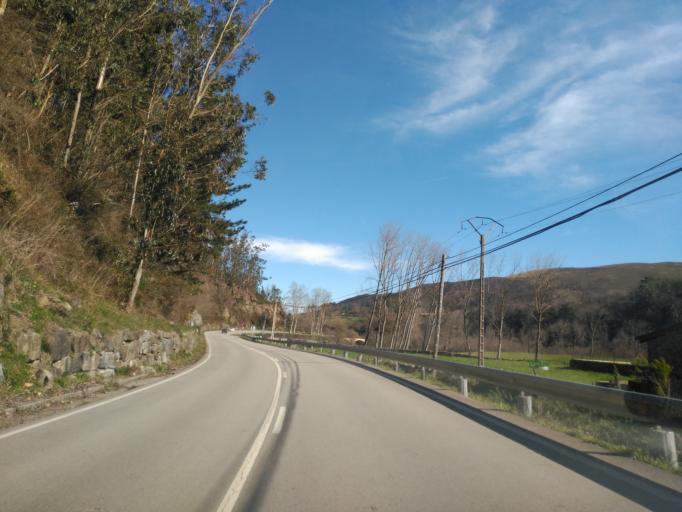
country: ES
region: Cantabria
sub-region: Provincia de Cantabria
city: Ruente
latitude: 43.2350
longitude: -4.2918
